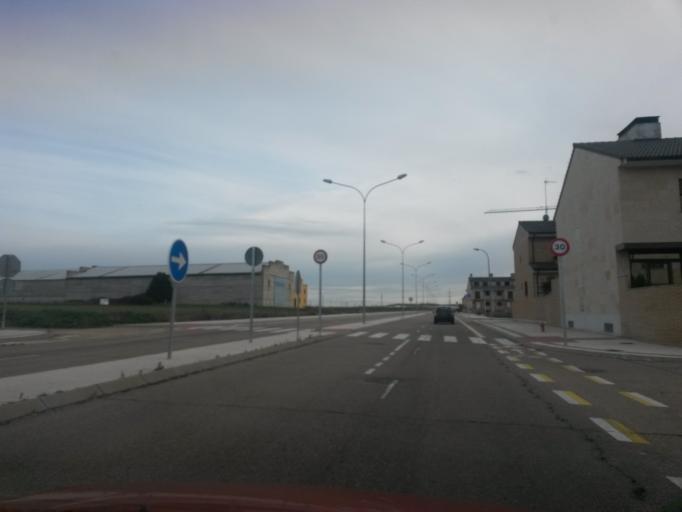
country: ES
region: Castille and Leon
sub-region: Provincia de Salamanca
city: Villares de la Reina
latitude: 41.0085
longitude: -5.6439
